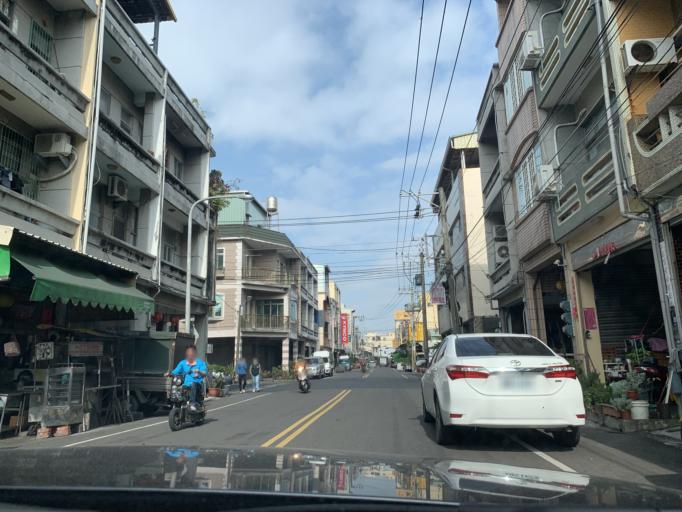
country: TW
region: Taiwan
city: Fengshan
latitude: 22.4666
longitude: 120.4469
